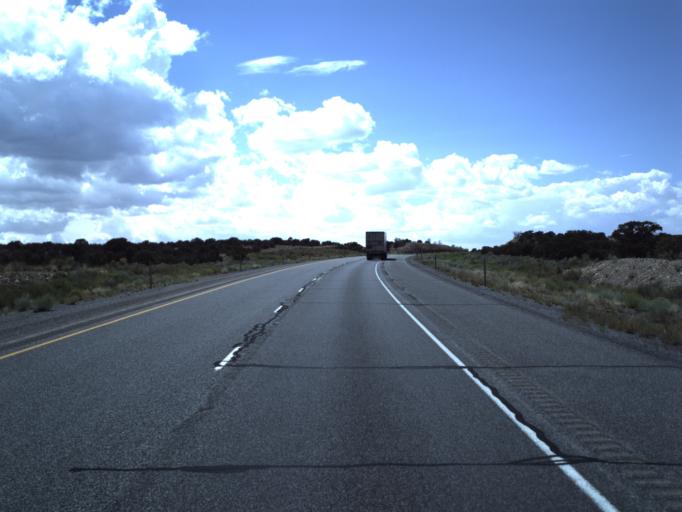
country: US
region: Utah
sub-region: Emery County
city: Castle Dale
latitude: 38.8990
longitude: -110.5752
